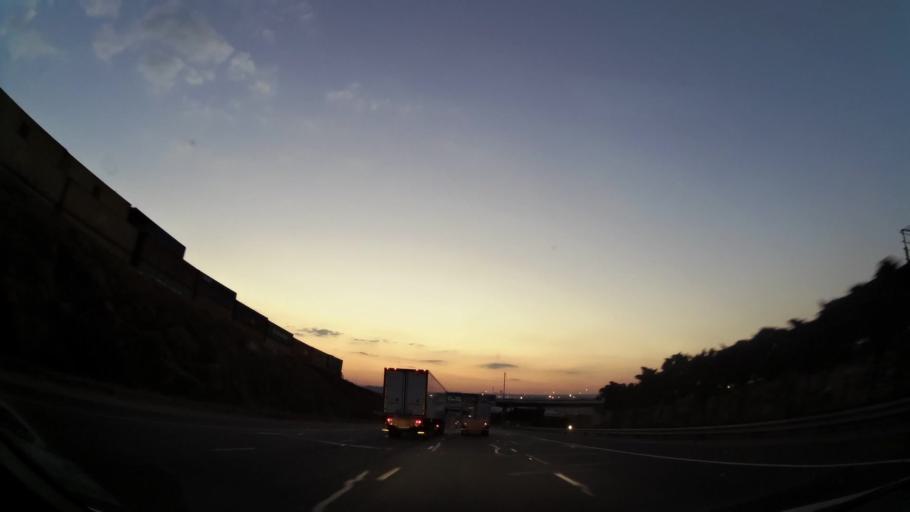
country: ZA
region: Gauteng
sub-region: Ekurhuleni Metropolitan Municipality
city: Germiston
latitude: -26.2478
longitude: 28.1345
